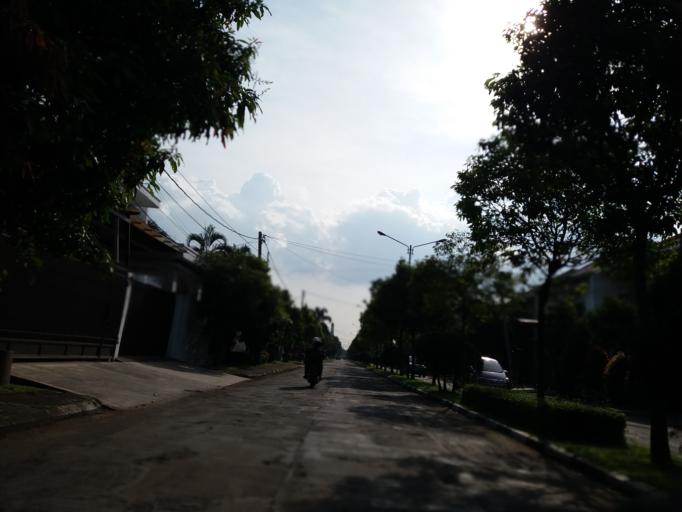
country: ID
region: West Java
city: Bandung
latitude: -6.9595
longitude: 107.6297
